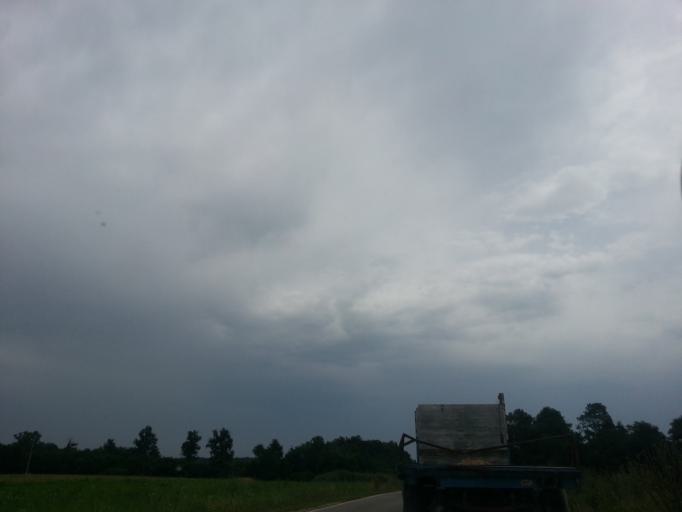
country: BA
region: Republika Srpska
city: Velika Obarska
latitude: 44.8046
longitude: 19.0733
